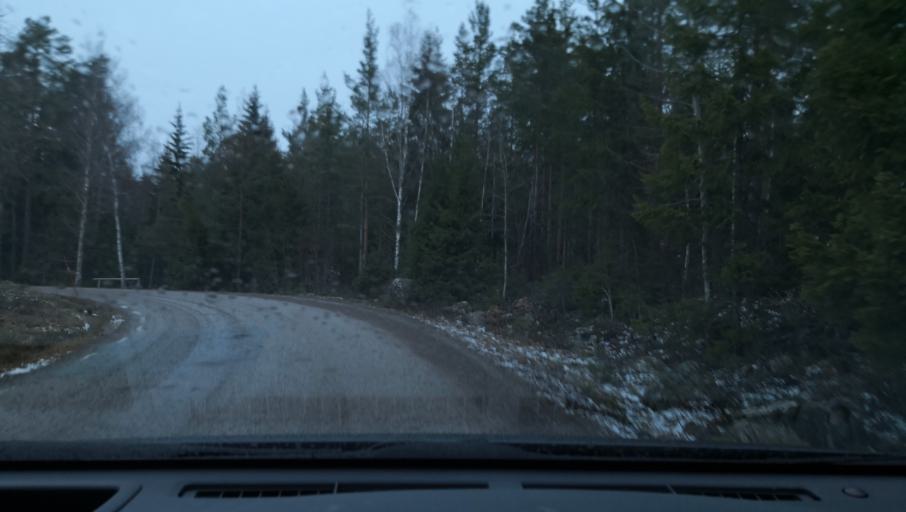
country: SE
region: Uppsala
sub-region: Enkopings Kommun
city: Hummelsta
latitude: 59.4593
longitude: 16.8460
